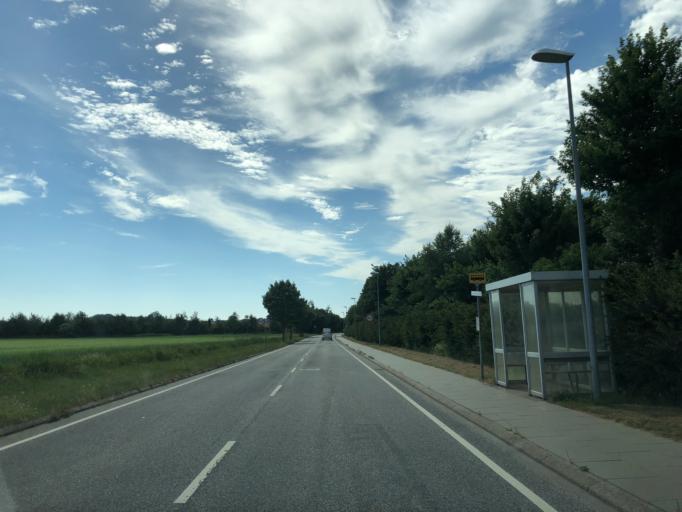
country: DK
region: Central Jutland
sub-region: Herning Kommune
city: Snejbjerg
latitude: 56.1260
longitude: 8.9054
